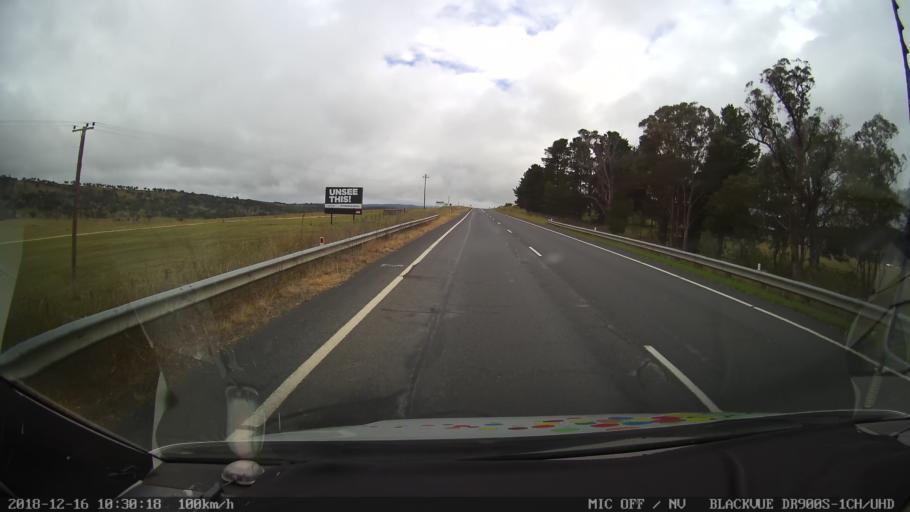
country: AU
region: New South Wales
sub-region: Tenterfield Municipality
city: Carrolls Creek
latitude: -29.0953
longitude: 152.0022
